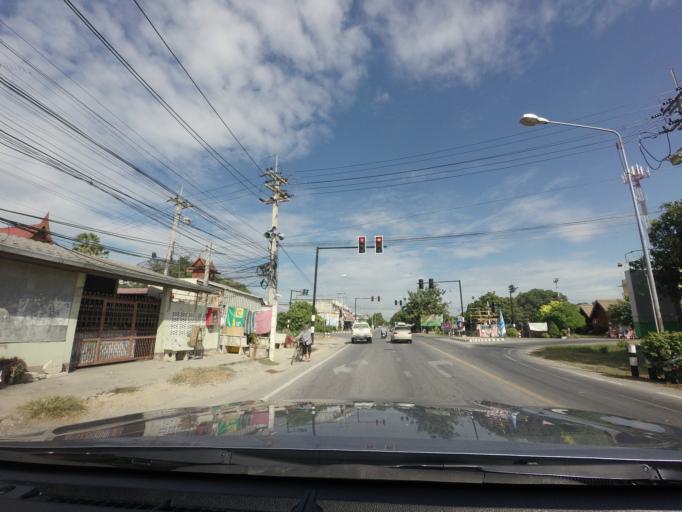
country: TH
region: Suphan Buri
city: Suphan Buri
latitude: 14.5376
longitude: 100.1271
